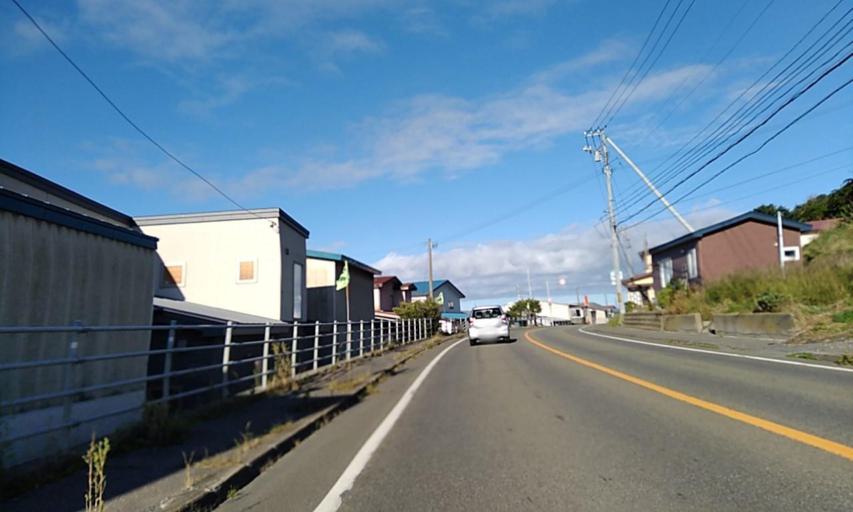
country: JP
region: Hokkaido
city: Shizunai-furukawacho
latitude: 42.1769
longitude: 142.7376
